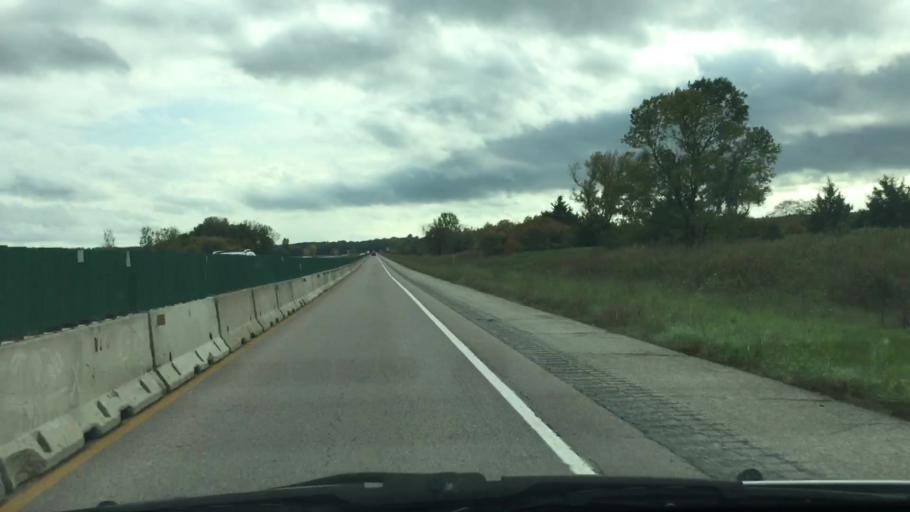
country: US
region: Iowa
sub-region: Decatur County
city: Lamoni
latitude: 40.6796
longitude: -93.8483
